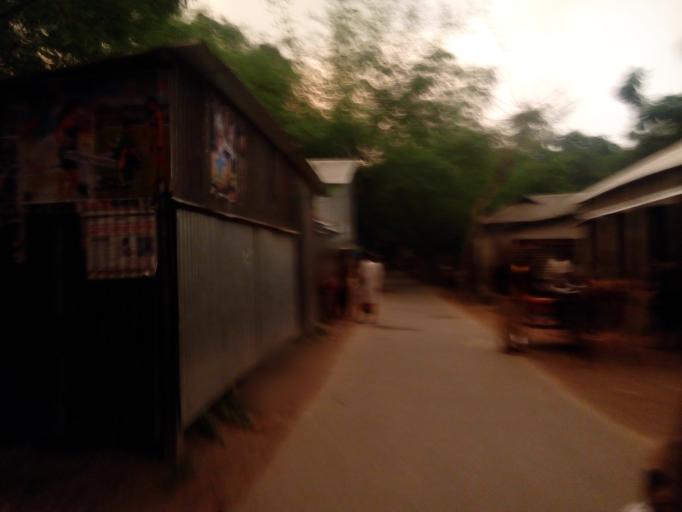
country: BD
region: Rajshahi
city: Sirajganj
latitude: 24.3032
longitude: 89.6908
